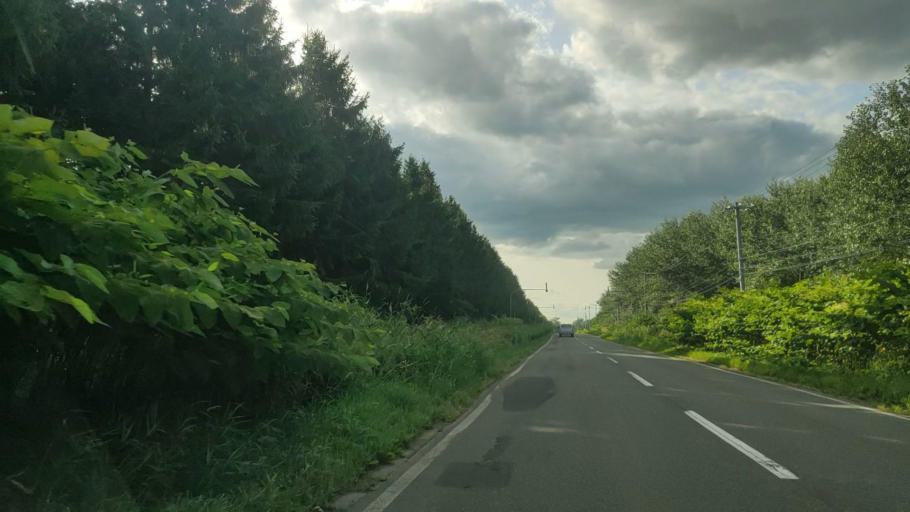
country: JP
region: Hokkaido
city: Makubetsu
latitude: 44.9001
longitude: 141.9124
